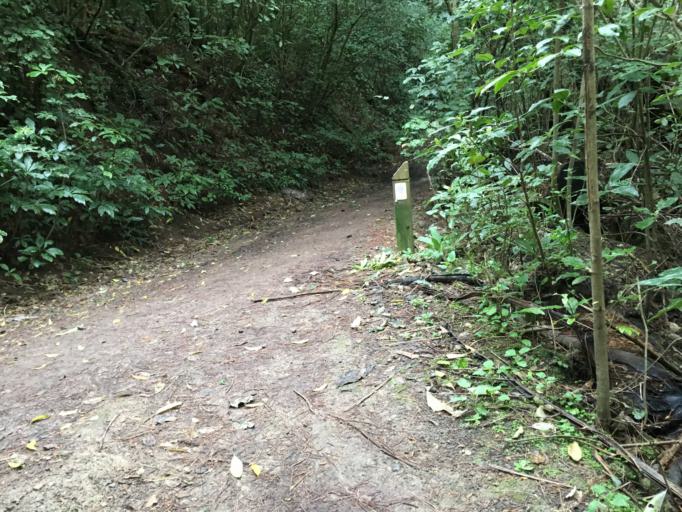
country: NZ
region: Wellington
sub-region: Wellington City
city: Kelburn
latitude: -41.2701
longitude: 174.7689
